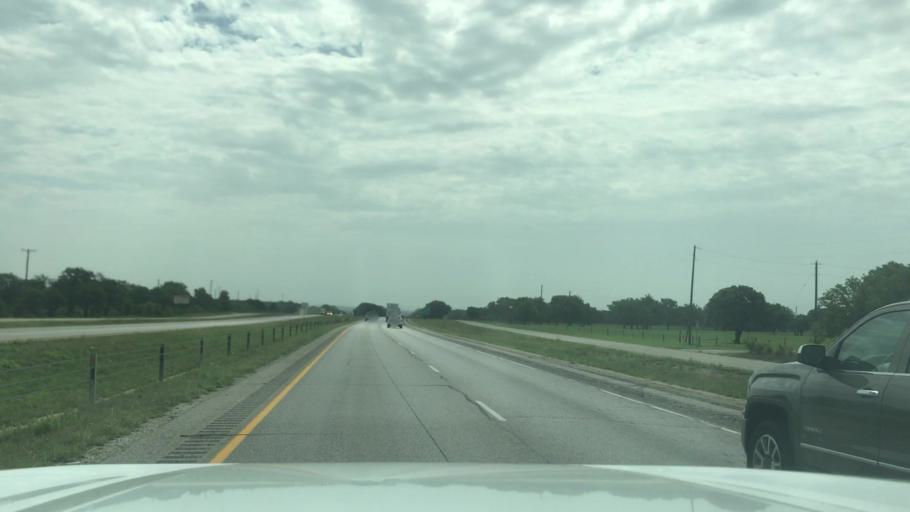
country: US
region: Texas
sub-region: Callahan County
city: Baird
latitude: 32.4061
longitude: -99.4428
